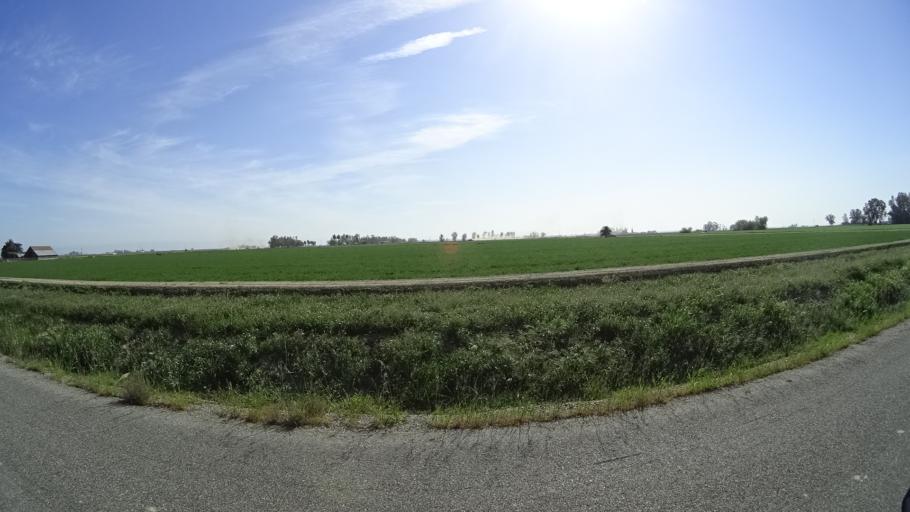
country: US
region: California
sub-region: Glenn County
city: Willows
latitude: 39.5798
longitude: -122.1170
